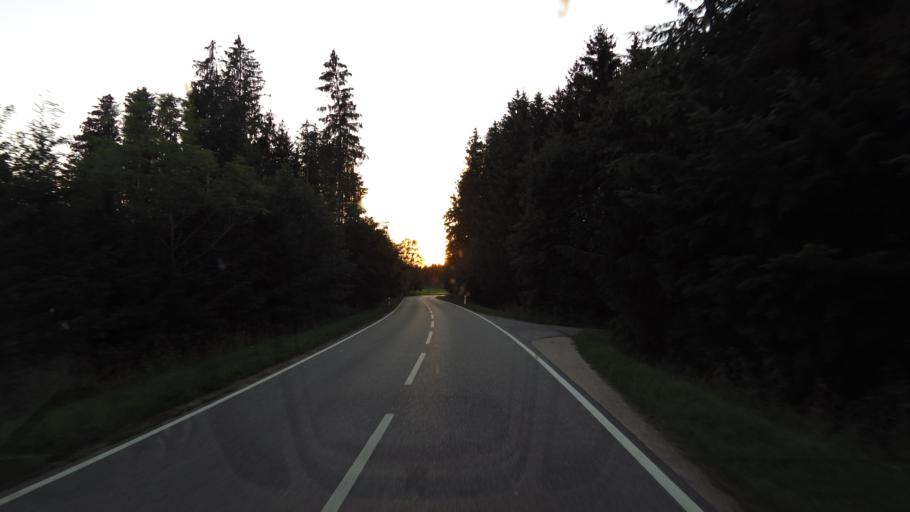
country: DE
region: Bavaria
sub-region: Upper Bavaria
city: Taufkirchen
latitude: 48.1513
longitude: 12.4488
